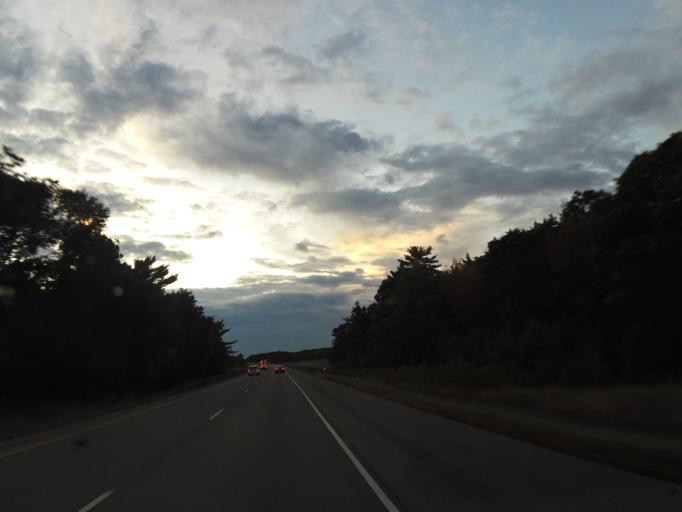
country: US
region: Wisconsin
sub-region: Juneau County
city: New Lisbon
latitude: 43.9477
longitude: -90.3243
